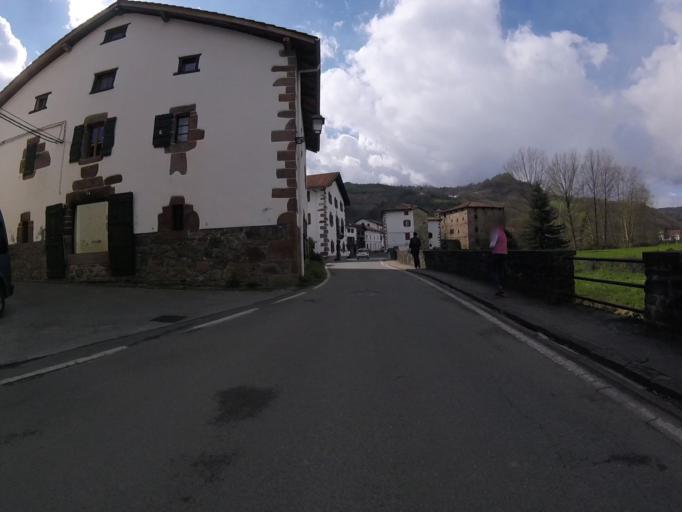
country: ES
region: Navarre
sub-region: Provincia de Navarra
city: Etxalar
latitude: 43.2352
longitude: -1.6359
